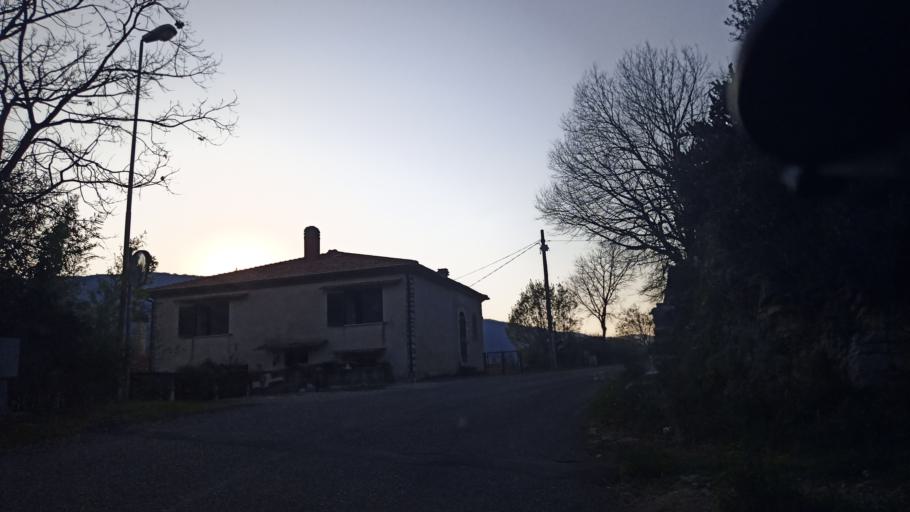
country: IT
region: Latium
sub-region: Provincia di Rieti
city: Cottanello
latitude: 42.4108
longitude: 12.6804
